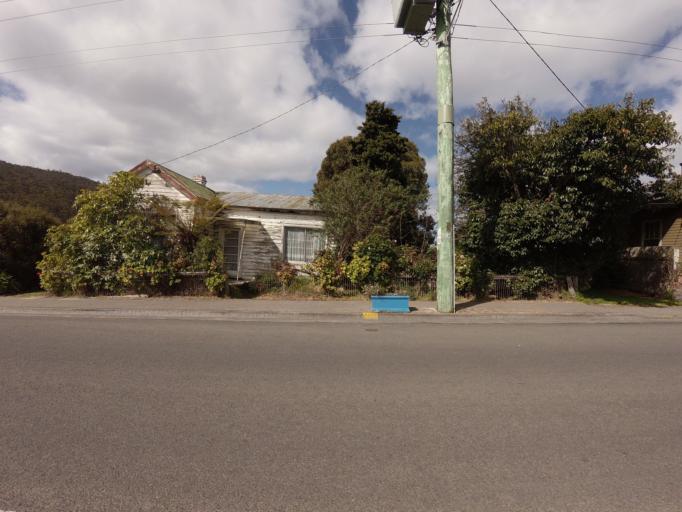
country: AU
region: Tasmania
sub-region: Huon Valley
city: Cygnet
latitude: -43.3135
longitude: 147.0154
